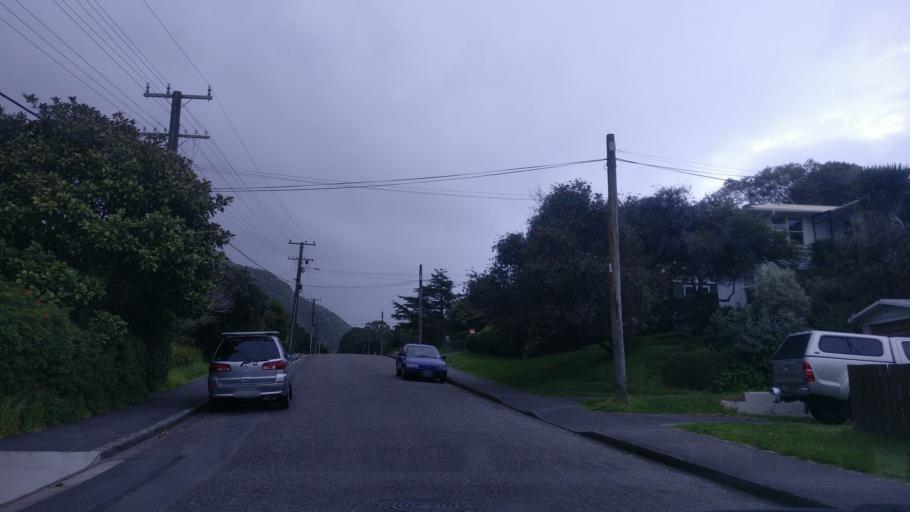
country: NZ
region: Wellington
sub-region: Kapiti Coast District
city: Paraparaumu
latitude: -40.9802
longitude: 174.9618
